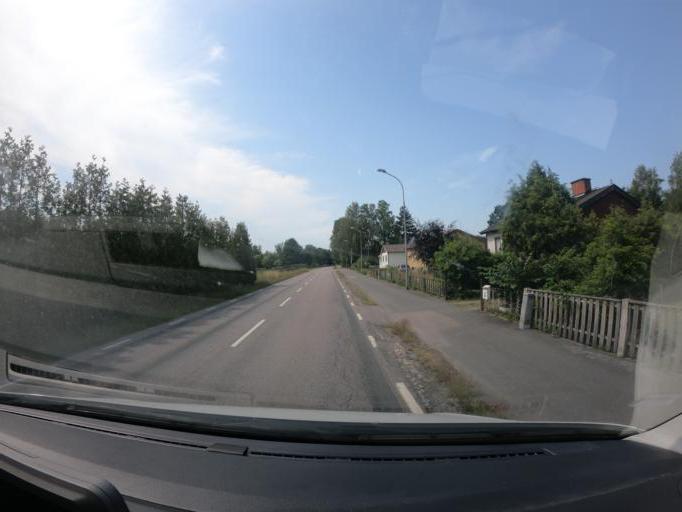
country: SE
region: Skane
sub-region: Hassleholms Kommun
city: Tormestorp
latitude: 56.1672
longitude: 13.6933
